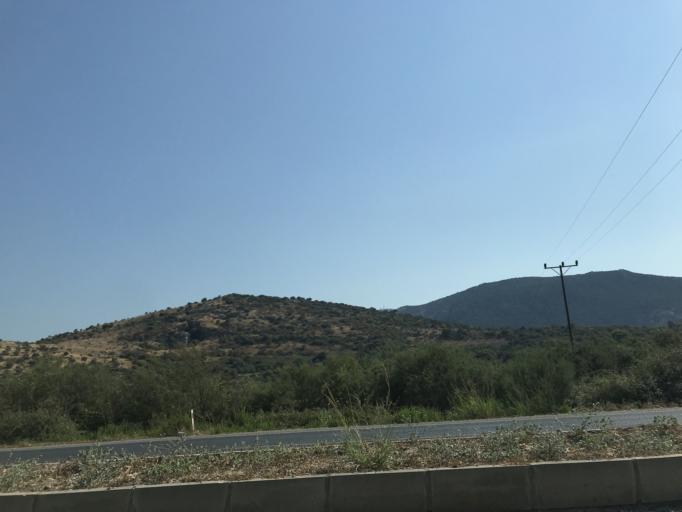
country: TR
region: Izmir
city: Selcuk
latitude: 37.9505
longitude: 27.3488
